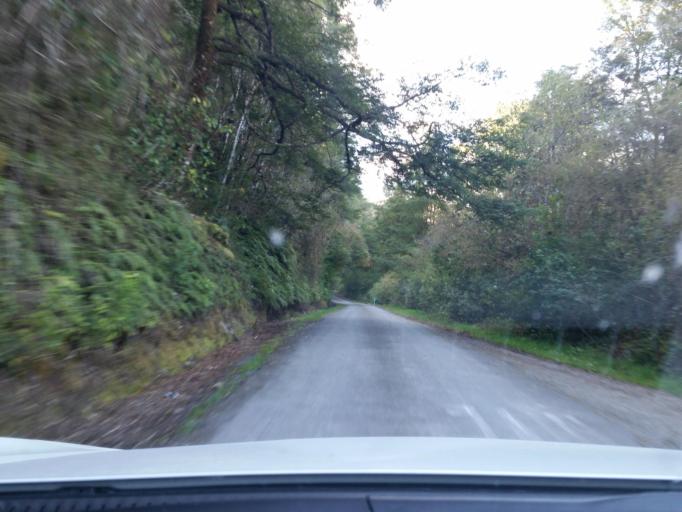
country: NZ
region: West Coast
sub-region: Buller District
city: Westport
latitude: -41.7774
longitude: 172.2174
